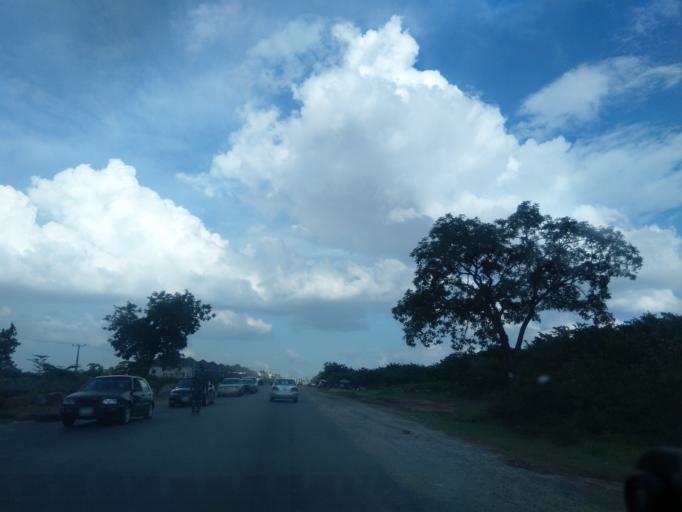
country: NG
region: Abuja Federal Capital Territory
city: Abuja
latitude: 9.0429
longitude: 7.3894
